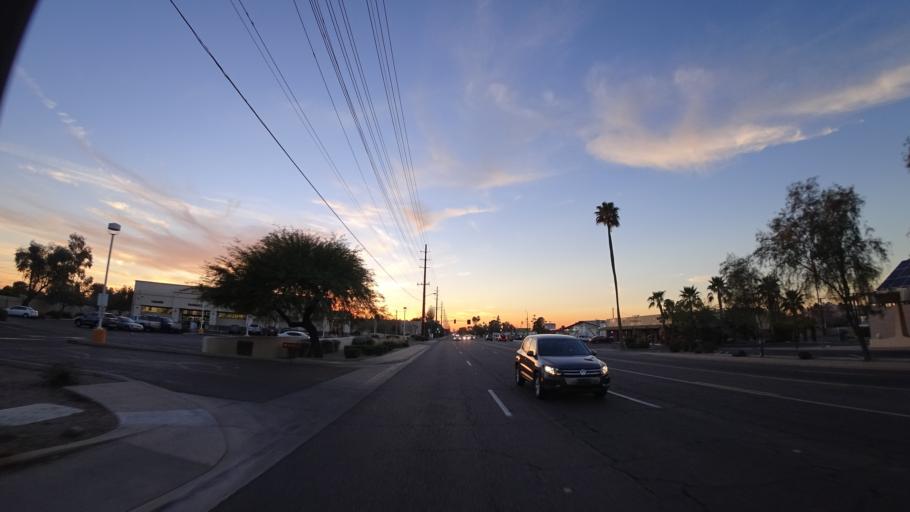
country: US
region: Arizona
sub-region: Maricopa County
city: Paradise Valley
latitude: 33.4799
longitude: -111.9597
